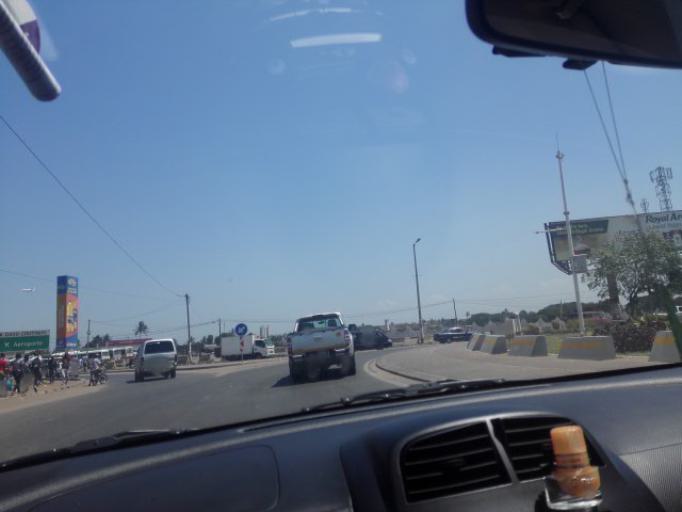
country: MZ
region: Maputo City
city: Maputo
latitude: -25.9344
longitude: 32.5509
